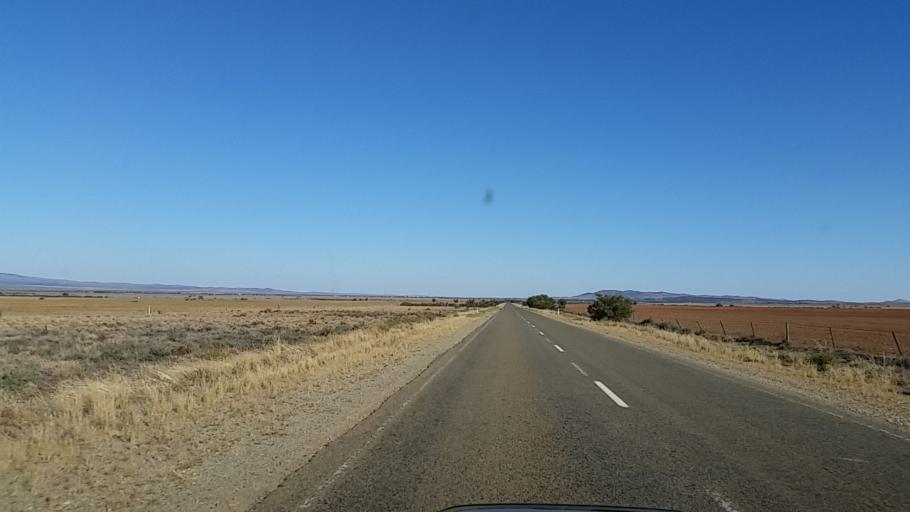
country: AU
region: South Australia
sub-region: Peterborough
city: Peterborough
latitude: -32.6526
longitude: 138.6022
